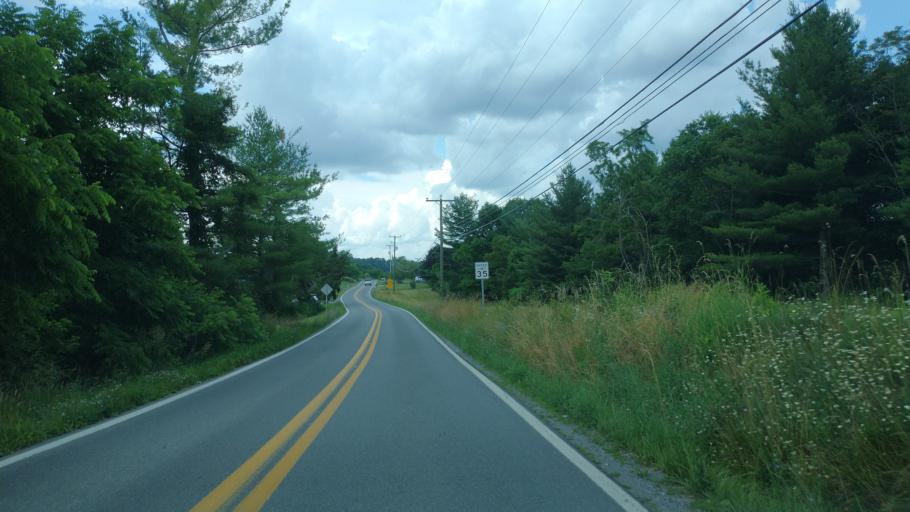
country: US
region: West Virginia
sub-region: Mercer County
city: Athens
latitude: 37.3951
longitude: -81.0595
